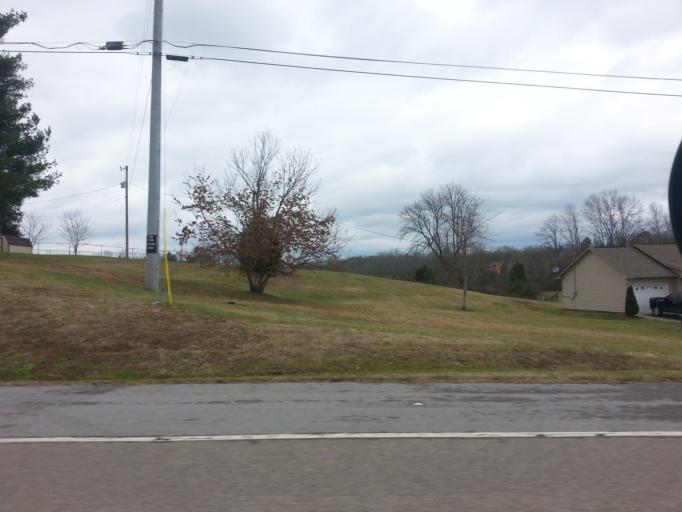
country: US
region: Tennessee
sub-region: Union County
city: Condon
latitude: 36.1513
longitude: -83.7552
